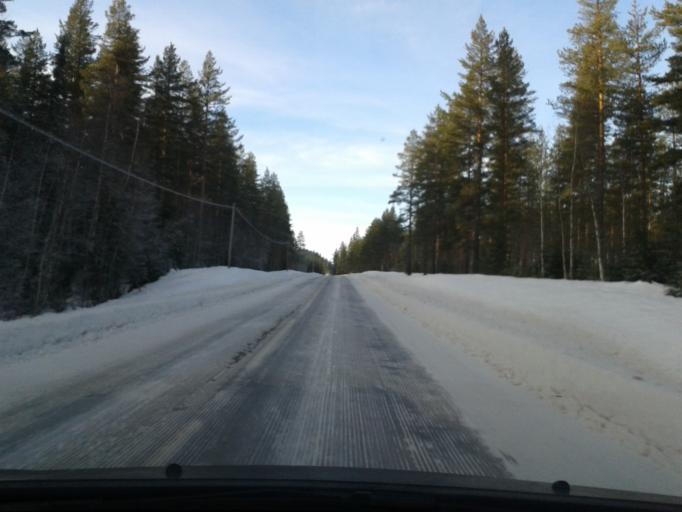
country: SE
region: Vaesternorrland
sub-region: OErnskoeldsviks Kommun
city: Bredbyn
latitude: 63.6648
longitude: 17.8355
